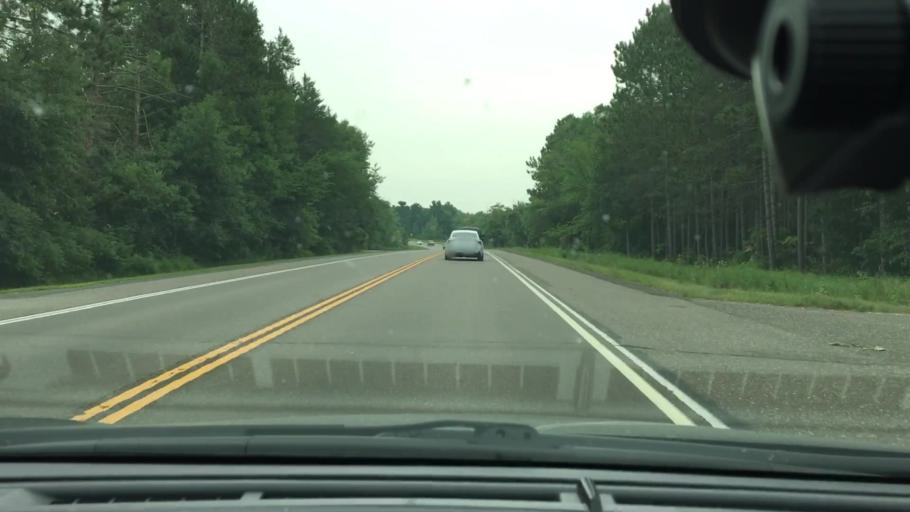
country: US
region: Minnesota
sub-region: Mille Lacs County
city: Vineland
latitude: 46.1164
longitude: -93.6623
